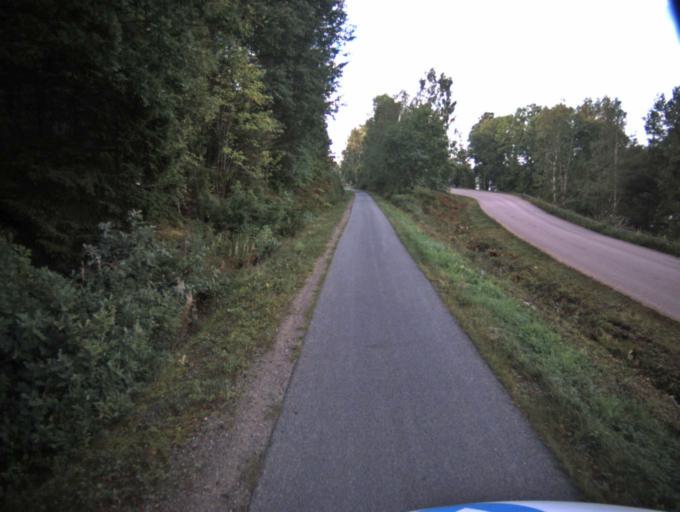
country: SE
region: Vaestra Goetaland
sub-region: Ulricehamns Kommun
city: Ulricehamn
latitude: 57.7529
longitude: 13.3955
